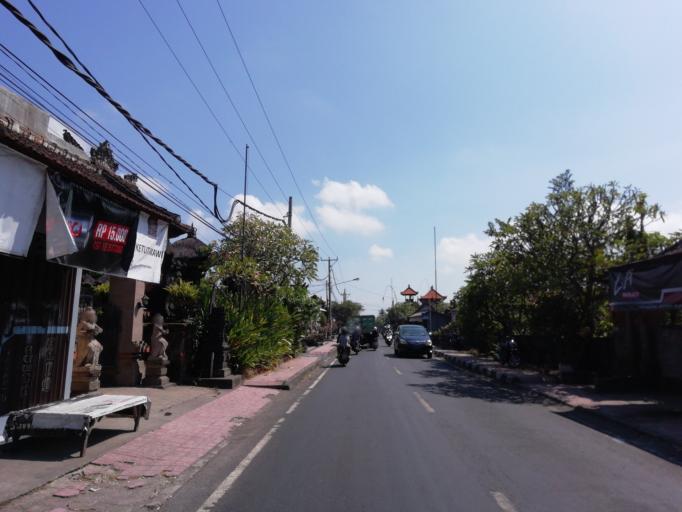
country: ID
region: Bali
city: Banjar Pasekan
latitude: -8.6285
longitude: 115.2844
